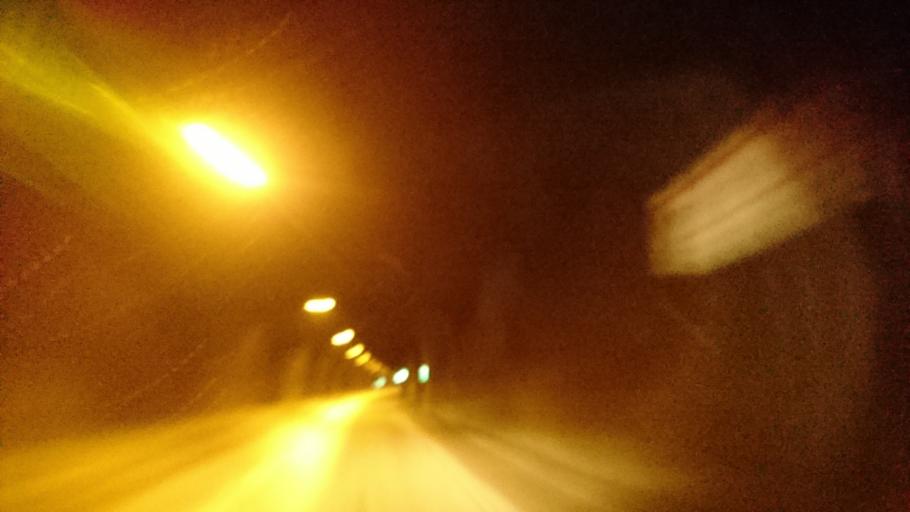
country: BO
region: La Paz
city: Coroico
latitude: -16.2708
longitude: -67.8301
